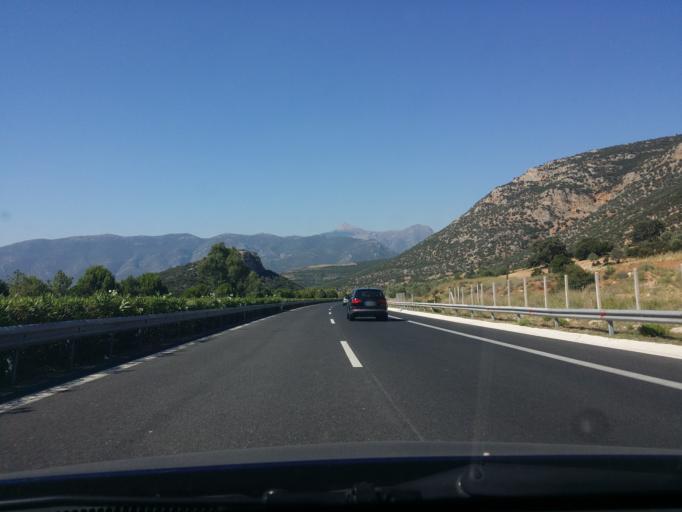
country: GR
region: Peloponnese
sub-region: Nomos Korinthias
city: Nemea
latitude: 37.7549
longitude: 22.6336
